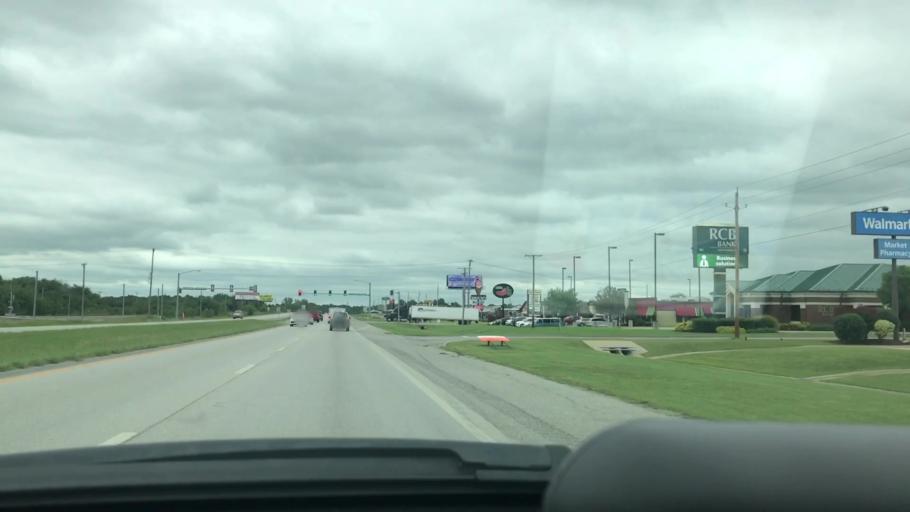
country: US
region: Oklahoma
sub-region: Mayes County
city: Pryor
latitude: 36.2620
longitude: -95.3332
